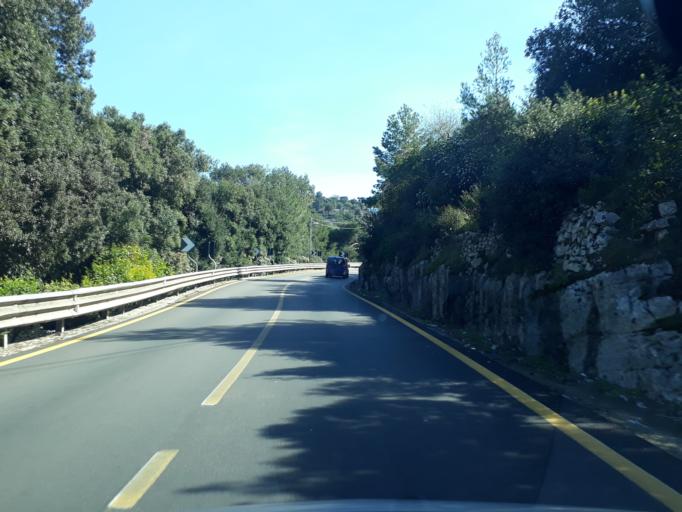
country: IT
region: Apulia
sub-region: Provincia di Brindisi
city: Lamie di Olimpie-Selva
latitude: 40.8052
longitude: 17.3498
